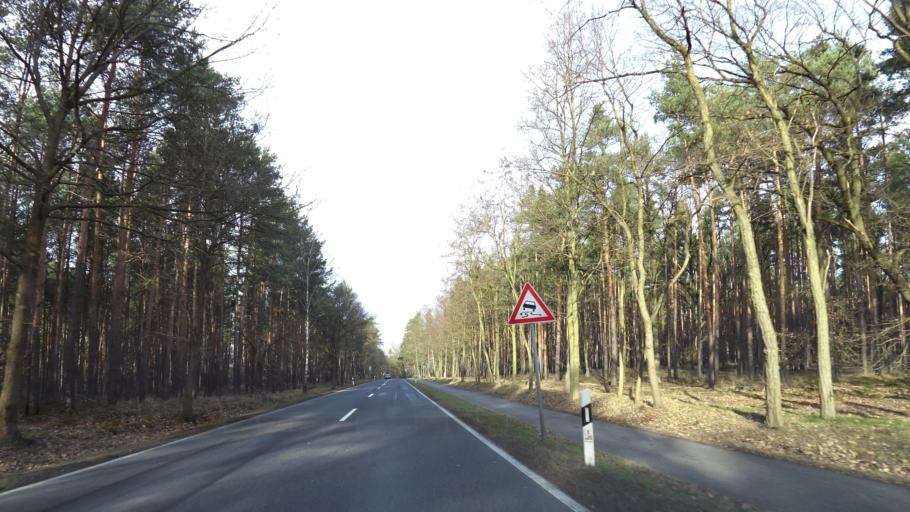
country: DE
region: Brandenburg
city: Michendorf
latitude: 52.3386
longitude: 13.0127
